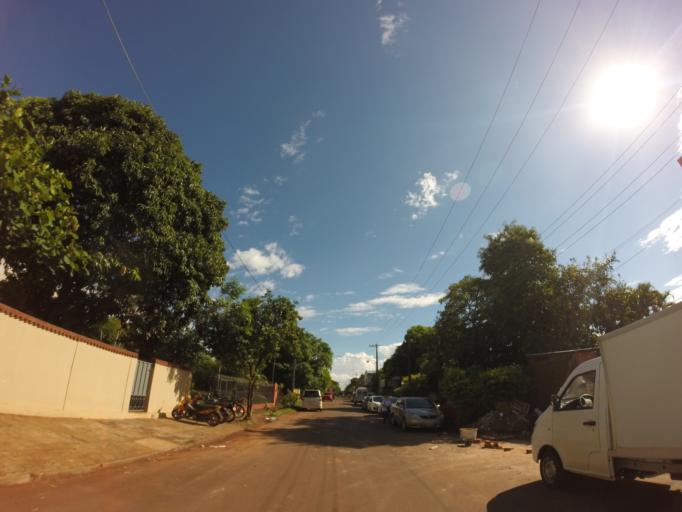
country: PY
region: Alto Parana
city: Ciudad del Este
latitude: -25.4054
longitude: -54.6259
